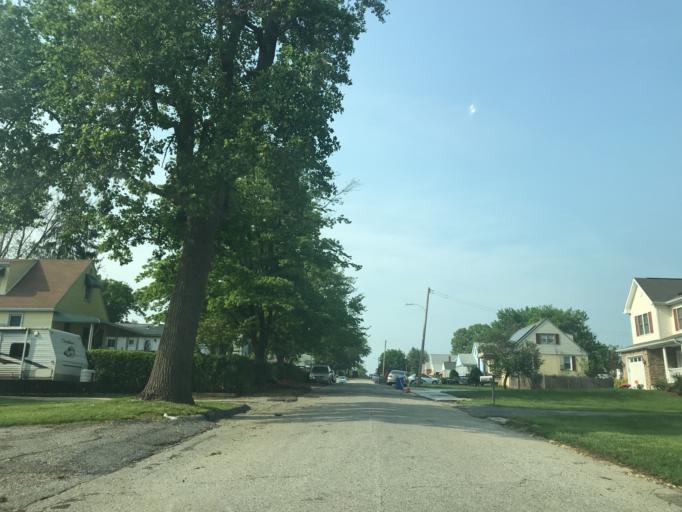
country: US
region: Maryland
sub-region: Baltimore County
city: Parkville
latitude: 39.3861
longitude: -76.5598
